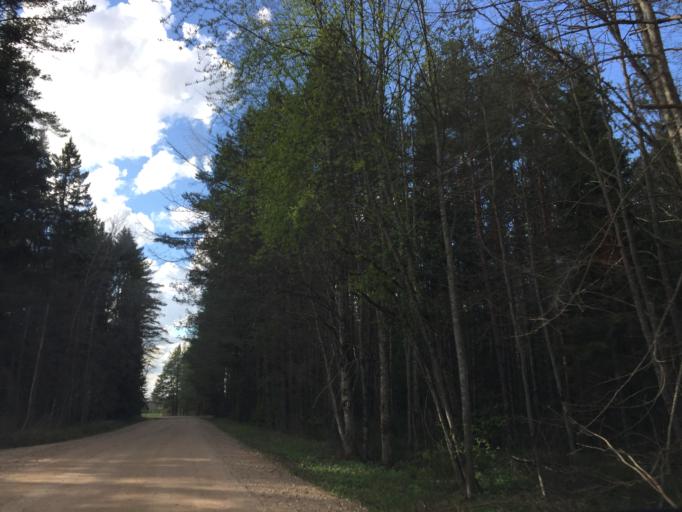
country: LV
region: Beverina
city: Murmuiza
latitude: 57.4719
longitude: 25.5304
